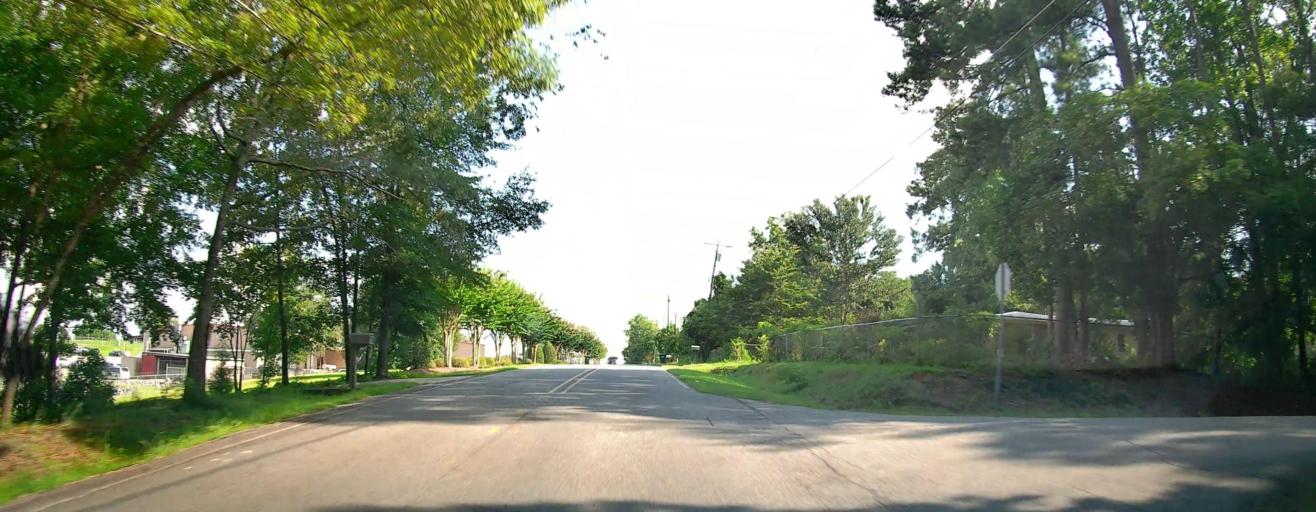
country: US
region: Georgia
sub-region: Houston County
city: Centerville
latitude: 32.6077
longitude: -83.6611
